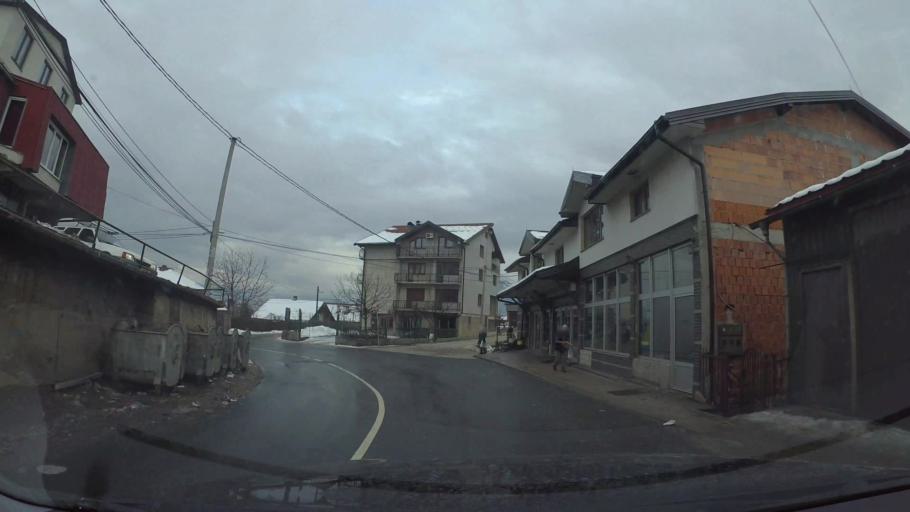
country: BA
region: Federation of Bosnia and Herzegovina
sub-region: Kanton Sarajevo
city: Sarajevo
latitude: 43.8577
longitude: 18.3574
